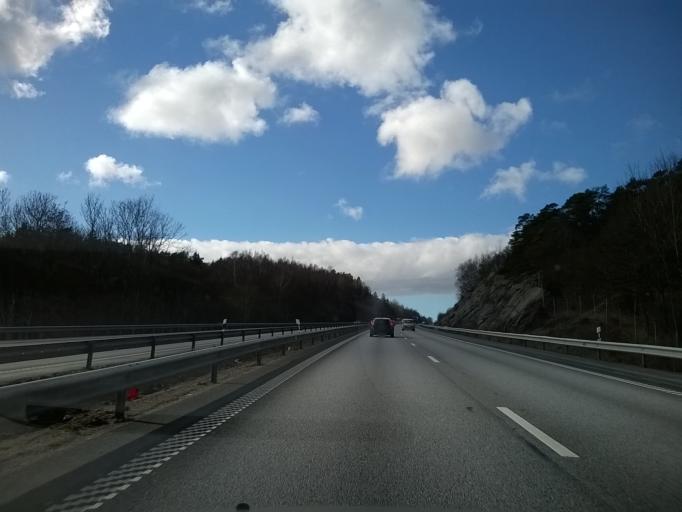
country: SE
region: Halland
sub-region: Kungsbacka Kommun
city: Fjaeras kyrkby
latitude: 57.4389
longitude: 12.1253
